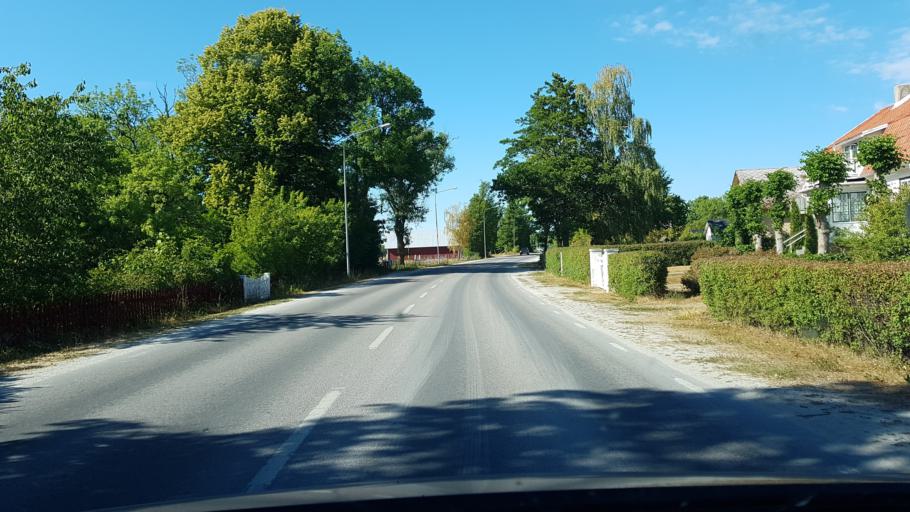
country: SE
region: Gotland
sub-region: Gotland
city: Klintehamn
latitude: 57.4380
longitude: 18.1447
